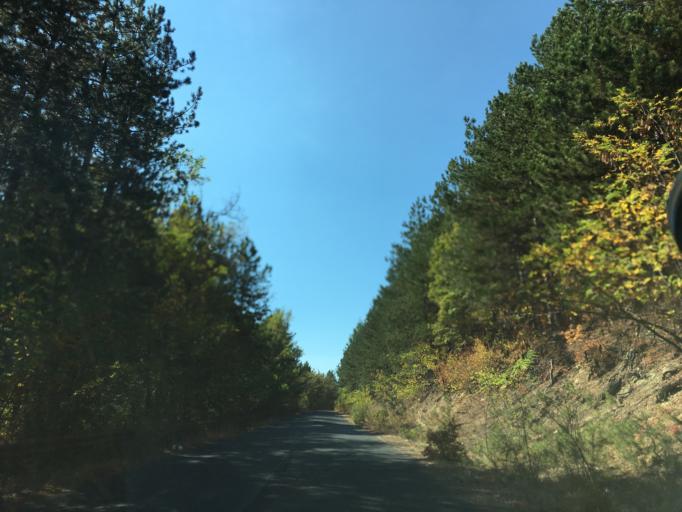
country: BG
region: Kurdzhali
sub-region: Obshtina Krumovgrad
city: Krumovgrad
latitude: 41.5514
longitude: 25.5568
